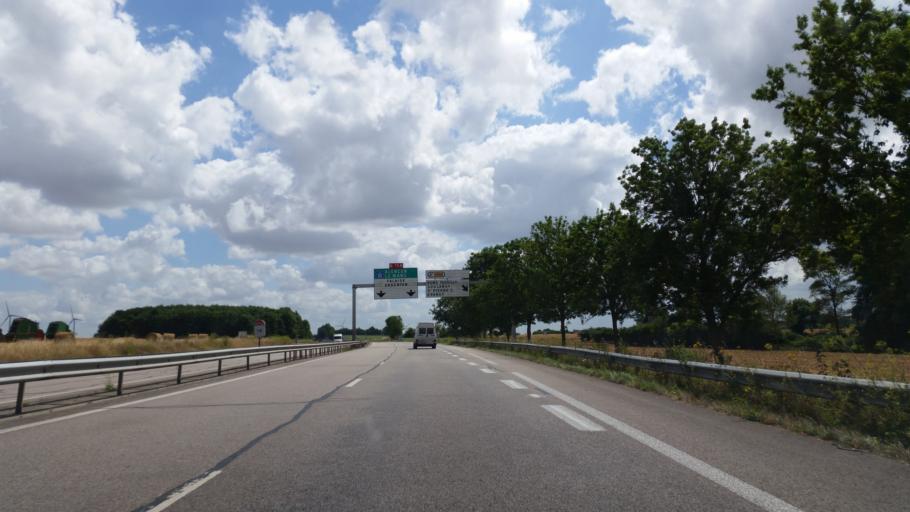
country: FR
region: Lower Normandy
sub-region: Departement du Calvados
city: Potigny
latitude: 48.9521
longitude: -0.2231
